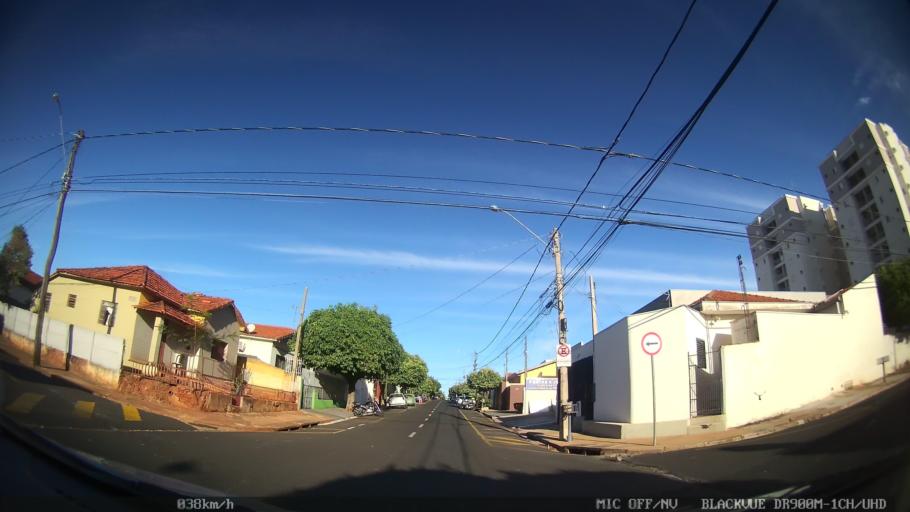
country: BR
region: Sao Paulo
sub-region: Sao Jose Do Rio Preto
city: Sao Jose do Rio Preto
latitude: -20.8262
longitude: -49.3788
